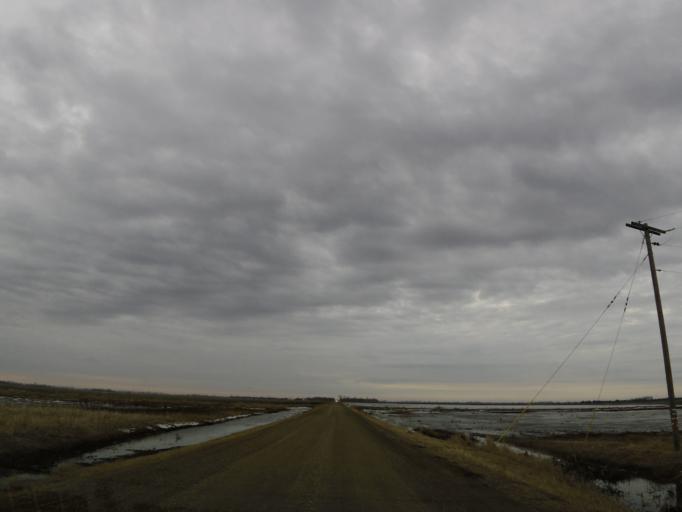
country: US
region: North Dakota
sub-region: Walsh County
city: Grafton
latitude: 48.3981
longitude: -97.4486
